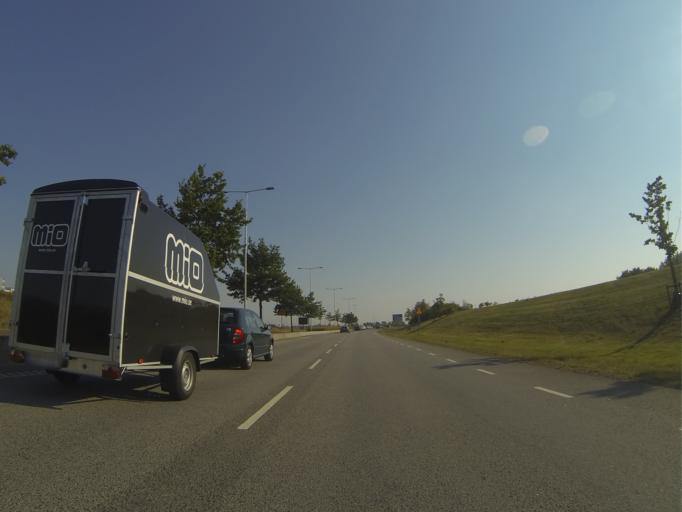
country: SE
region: Skane
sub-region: Malmo
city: Bunkeflostrand
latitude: 55.5679
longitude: 12.9688
